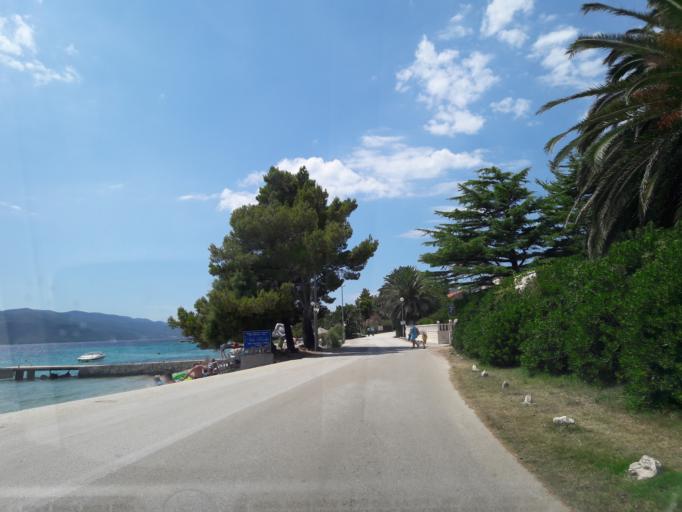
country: HR
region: Dubrovacko-Neretvanska
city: Korcula
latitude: 42.9745
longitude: 17.1397
